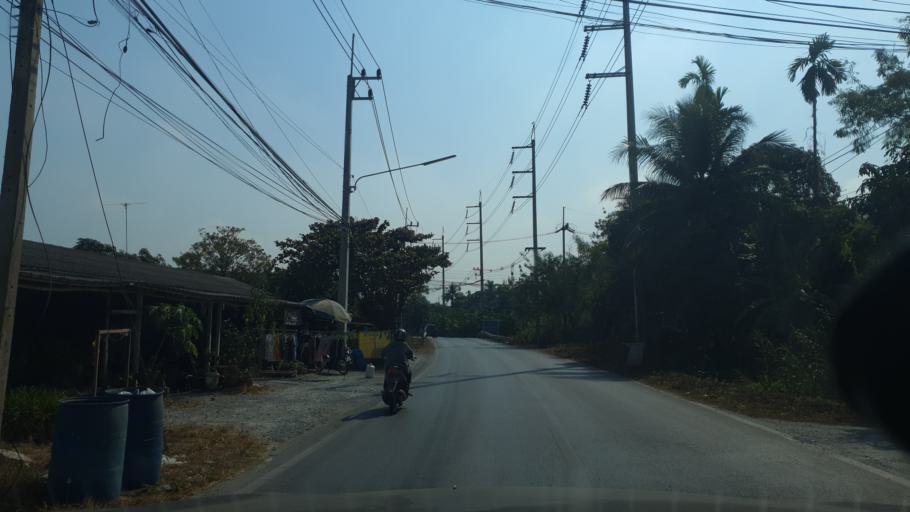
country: TH
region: Nakhon Pathom
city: Salaya
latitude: 13.7786
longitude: 100.2721
